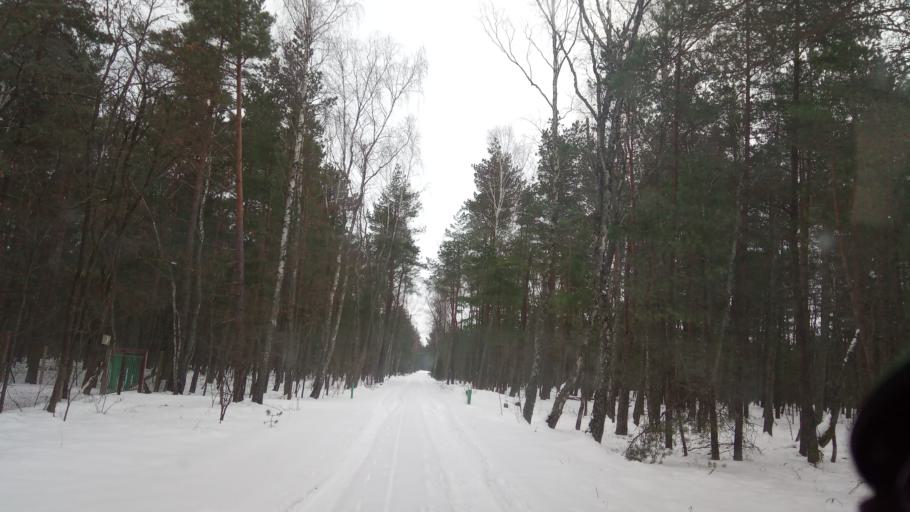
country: LT
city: Neringa
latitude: 55.4167
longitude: 21.0909
